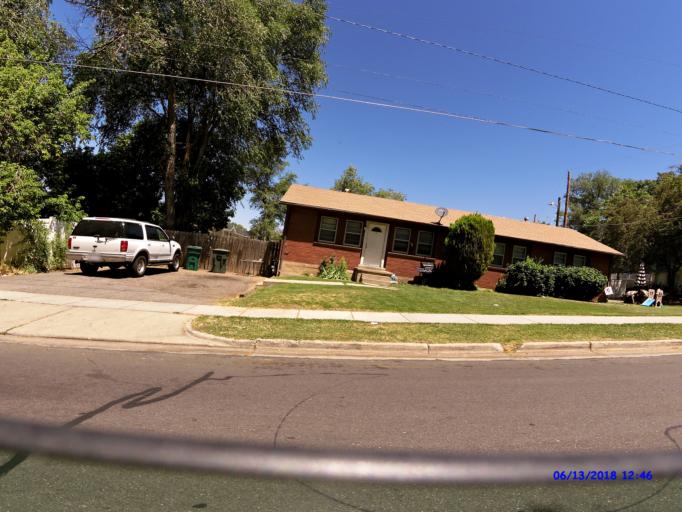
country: US
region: Utah
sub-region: Weber County
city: South Ogden
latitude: 41.2058
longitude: -111.9511
